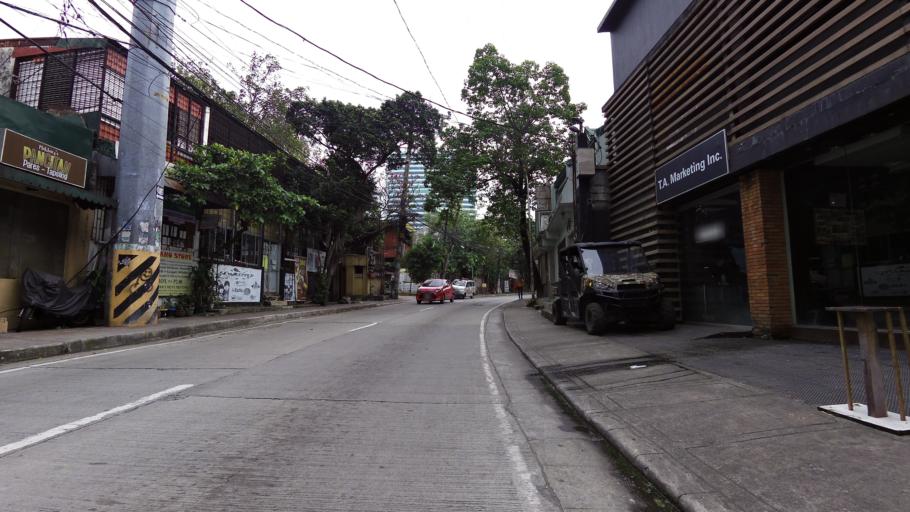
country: PH
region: Metro Manila
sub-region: San Juan
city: San Juan
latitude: 14.6163
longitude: 121.0512
